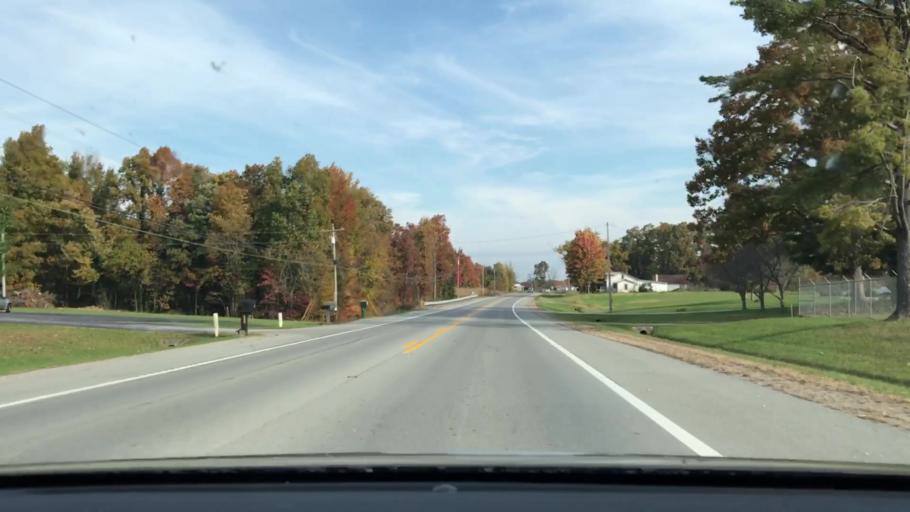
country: US
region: Tennessee
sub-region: Fentress County
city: Grimsley
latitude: 36.2755
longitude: -84.9820
